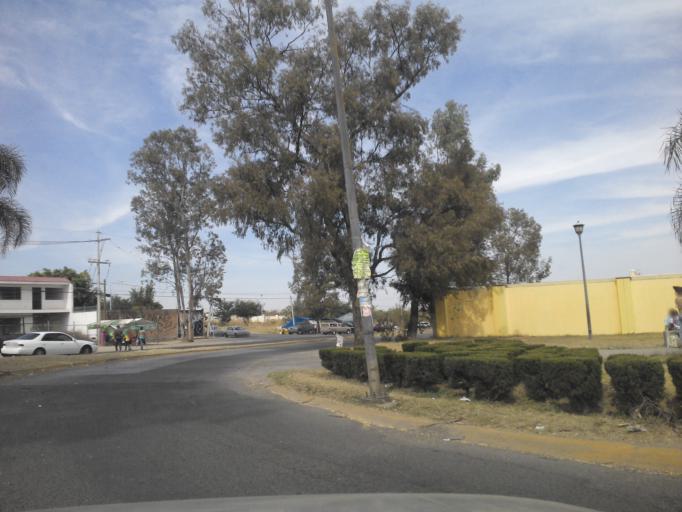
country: MX
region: Jalisco
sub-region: Tlajomulco de Zuniga
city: Lomas del Sur
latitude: 20.4989
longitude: -103.4159
